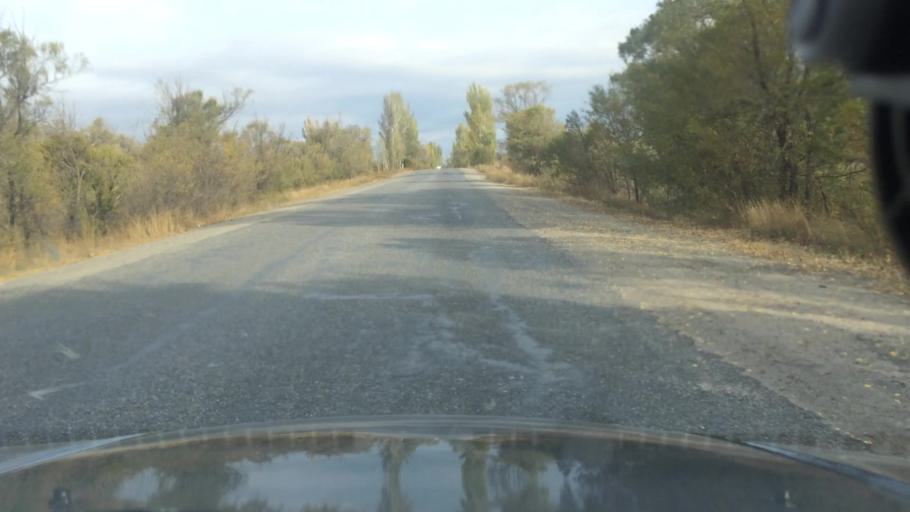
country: KG
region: Ysyk-Koel
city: Karakol
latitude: 42.5679
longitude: 78.3911
